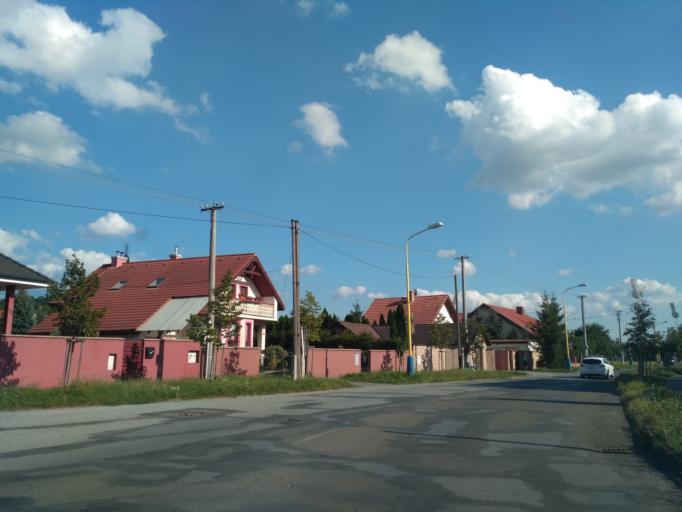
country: SK
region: Presovsky
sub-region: Okres Presov
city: Presov
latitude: 49.0101
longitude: 21.2329
